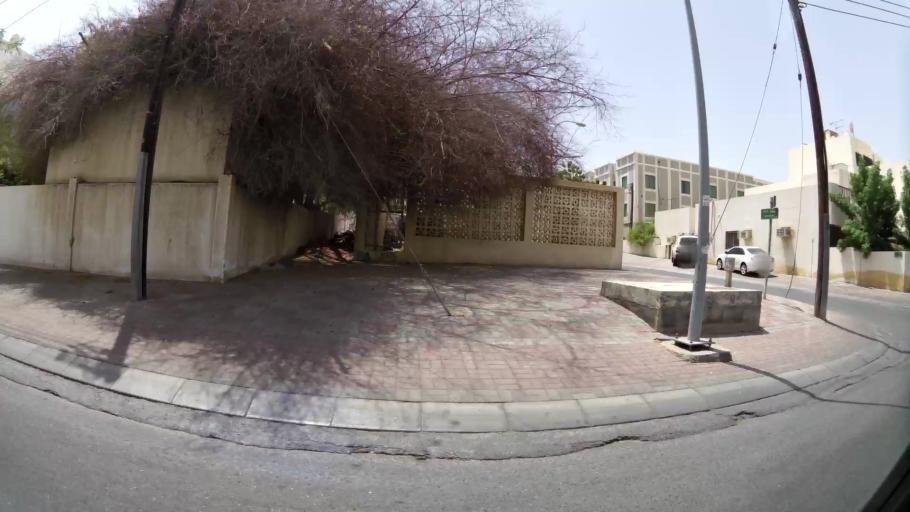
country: OM
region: Muhafazat Masqat
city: Bawshar
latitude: 23.5900
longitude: 58.4368
